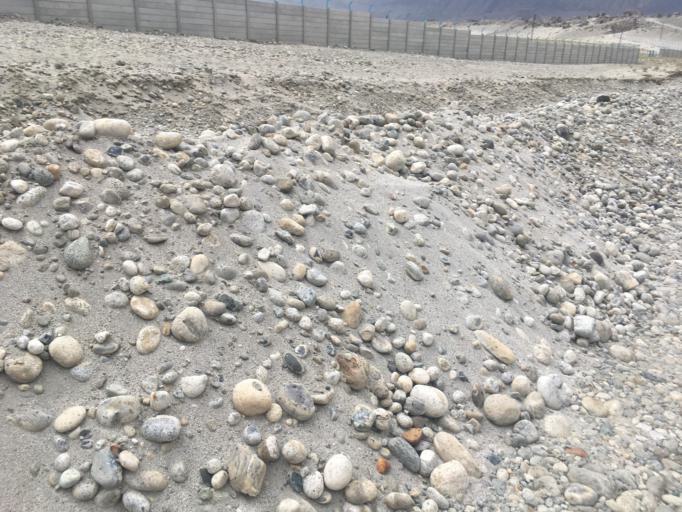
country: PK
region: Gilgit-Baltistan
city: Skardu
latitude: 35.3153
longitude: 75.6575
